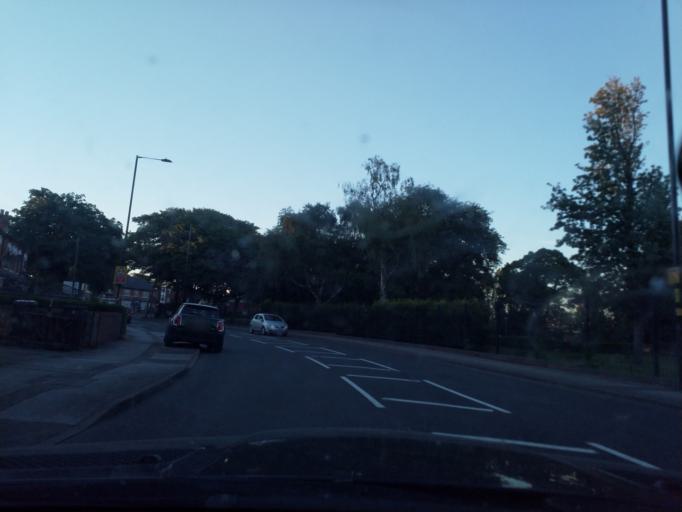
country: GB
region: England
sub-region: City and Borough of Birmingham
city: Acocks Green
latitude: 52.4580
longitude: -1.8182
